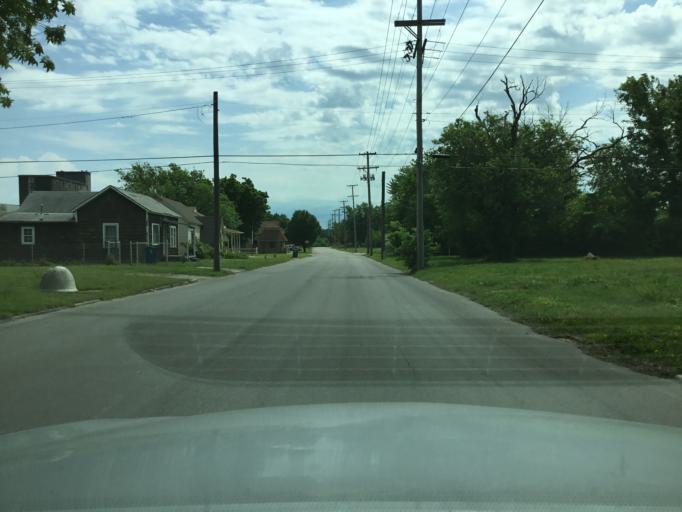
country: US
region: Kansas
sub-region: Montgomery County
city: Coffeyville
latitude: 37.0288
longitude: -95.6205
